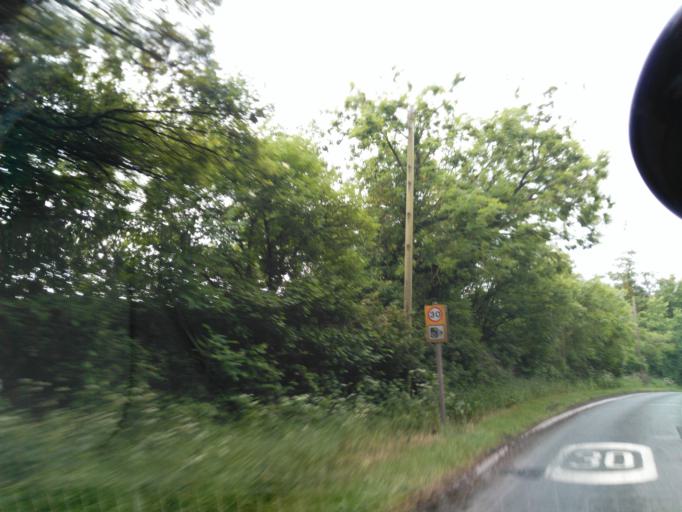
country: GB
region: England
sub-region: Somerset
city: Shepton Mallet
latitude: 51.1642
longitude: -2.5933
